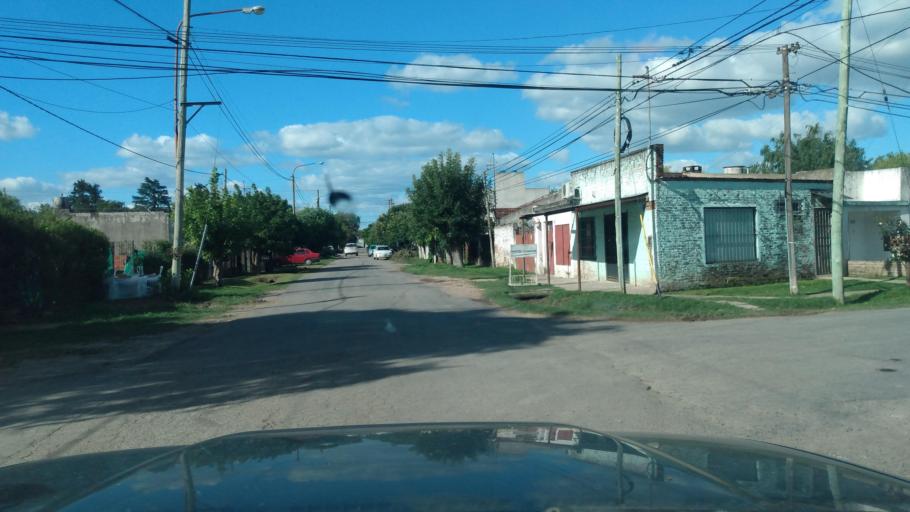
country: AR
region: Buenos Aires
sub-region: Partido de Lujan
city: Lujan
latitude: -34.5835
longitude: -59.0959
